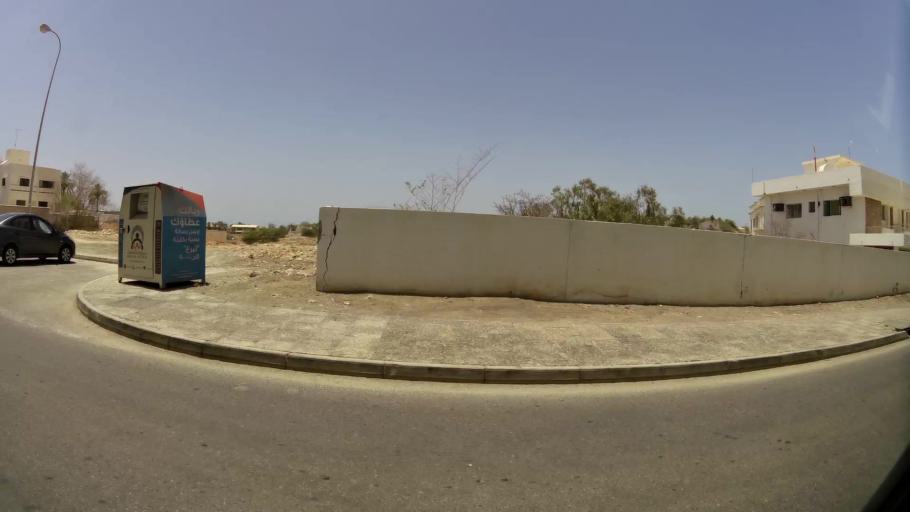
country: OM
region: Muhafazat Masqat
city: Muscat
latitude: 23.6251
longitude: 58.4971
